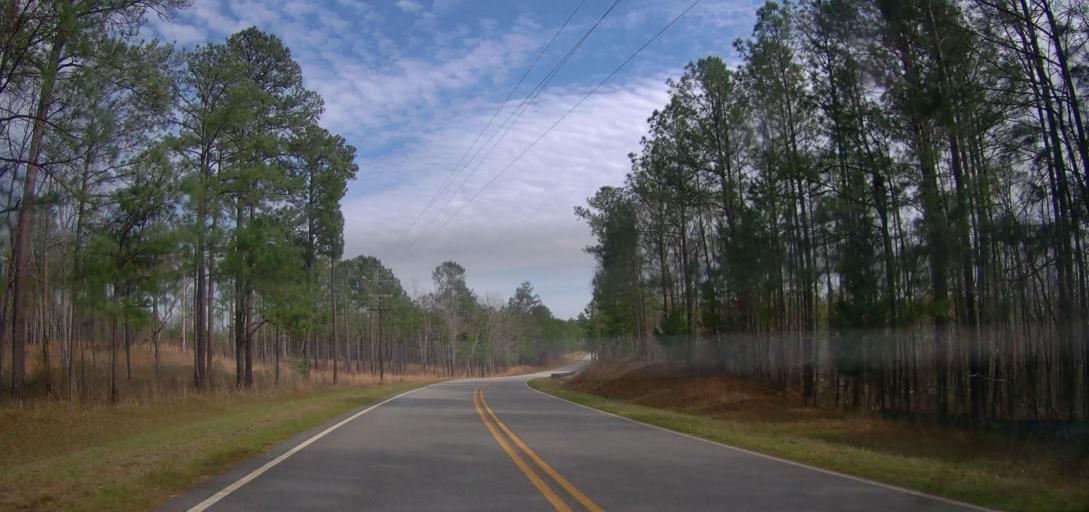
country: US
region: Georgia
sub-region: Monroe County
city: Forsyth
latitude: 33.0713
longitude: -83.7350
